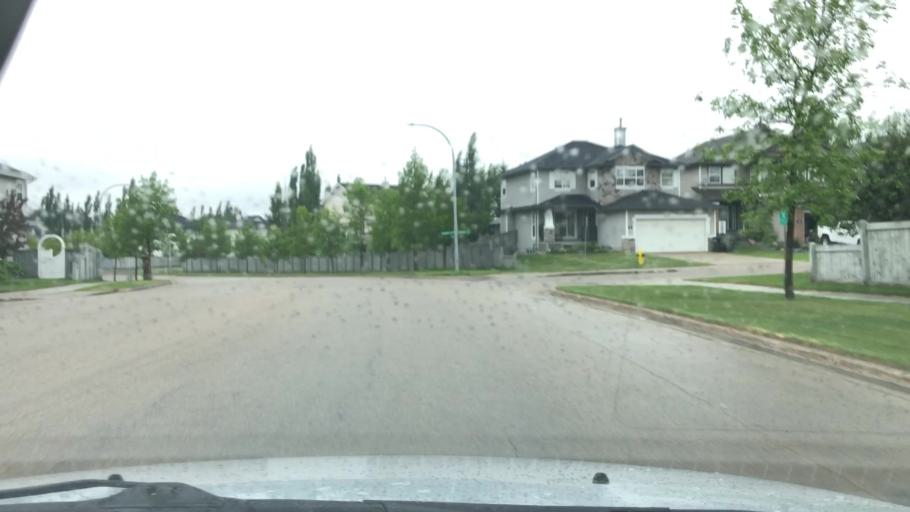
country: CA
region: Alberta
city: Sherwood Park
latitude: 53.5367
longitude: -113.2604
